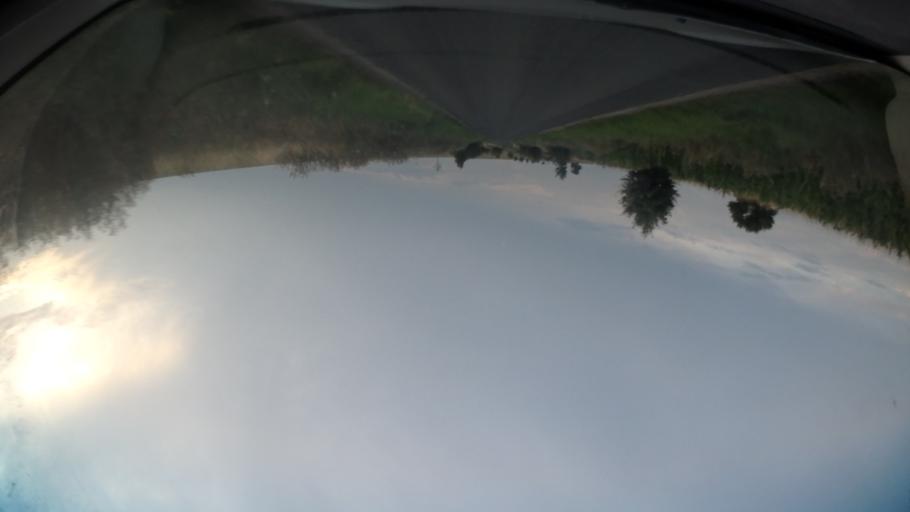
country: CZ
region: South Moravian
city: Orechov
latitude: 49.0901
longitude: 16.4980
